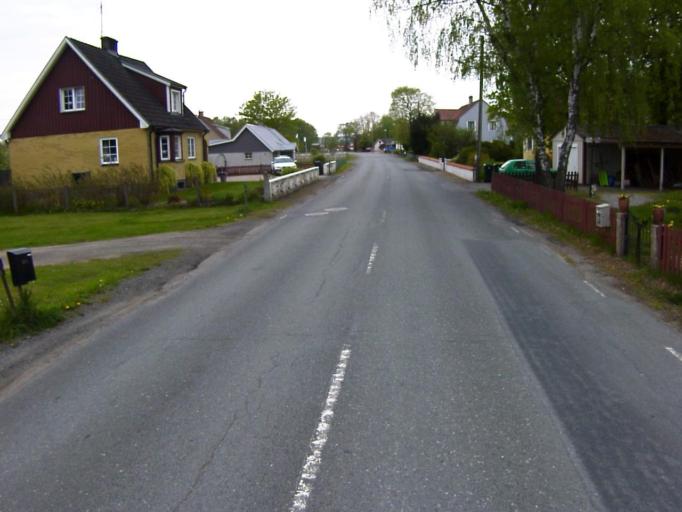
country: SE
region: Skane
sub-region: Kristianstads Kommun
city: Onnestad
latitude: 55.9319
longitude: 13.9969
